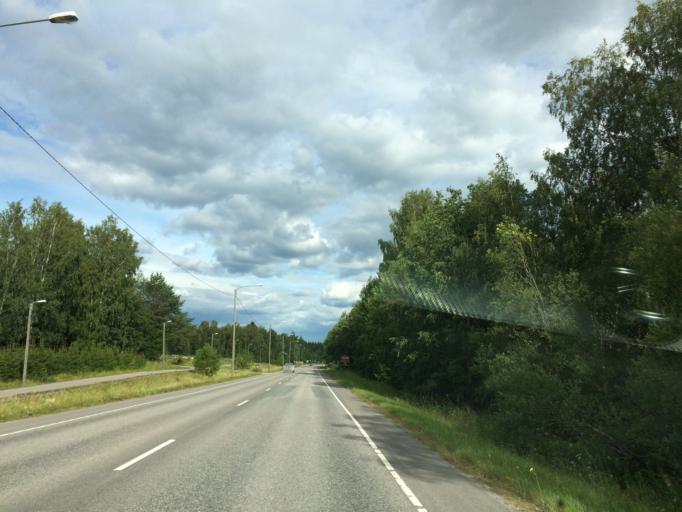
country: FI
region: Haeme
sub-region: Haemeenlinna
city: Janakkala
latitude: 60.9603
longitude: 24.5764
